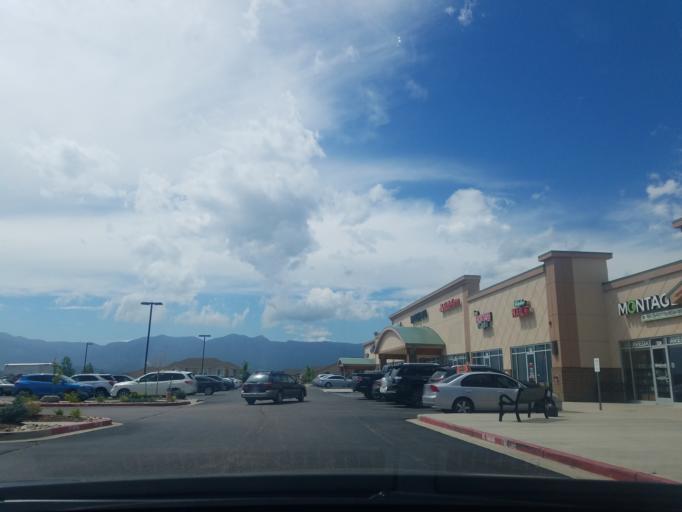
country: US
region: Colorado
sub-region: El Paso County
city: Gleneagle
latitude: 39.0023
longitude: -104.7986
